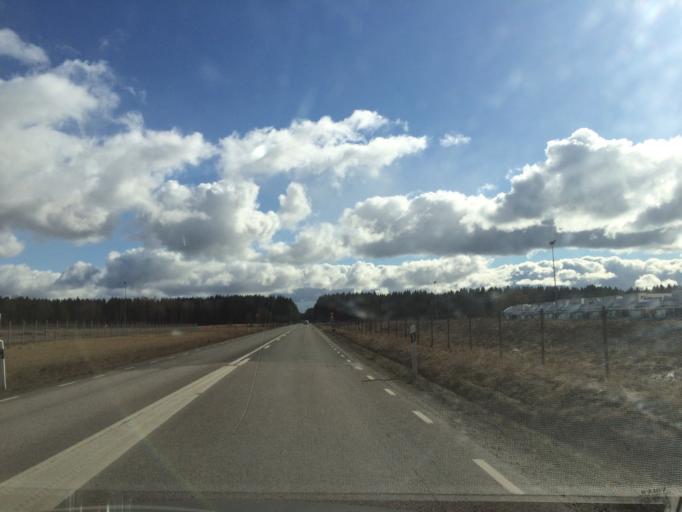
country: SE
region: Vaestra Goetaland
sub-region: Skara Kommun
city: Skara
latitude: 58.3720
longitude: 13.4155
